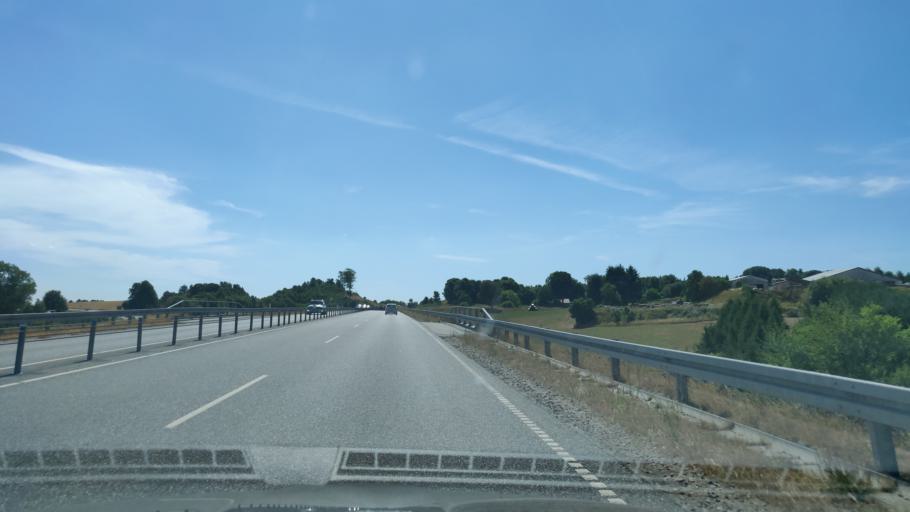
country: DK
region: Zealand
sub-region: Odsherred Kommune
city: Asnaes
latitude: 55.8162
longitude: 11.5835
